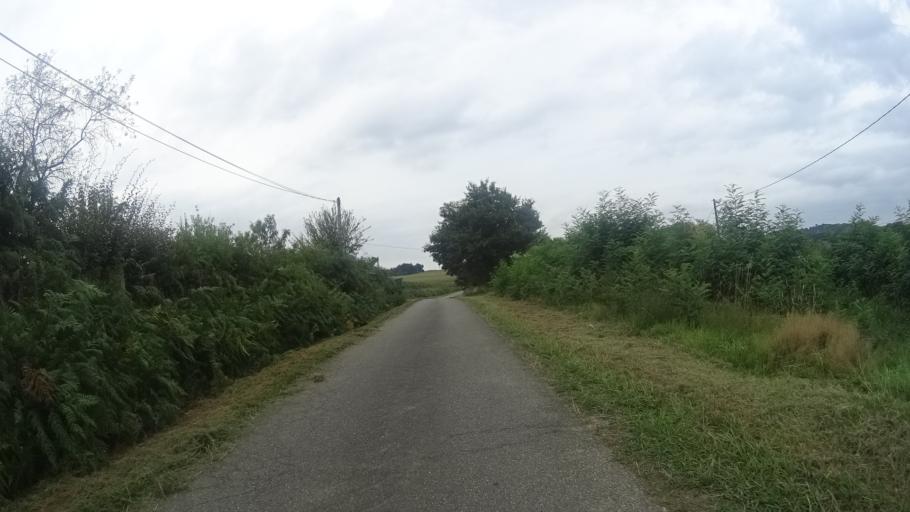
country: FR
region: Aquitaine
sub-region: Departement des Pyrenees-Atlantiques
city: Orthez
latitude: 43.4789
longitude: -0.7142
